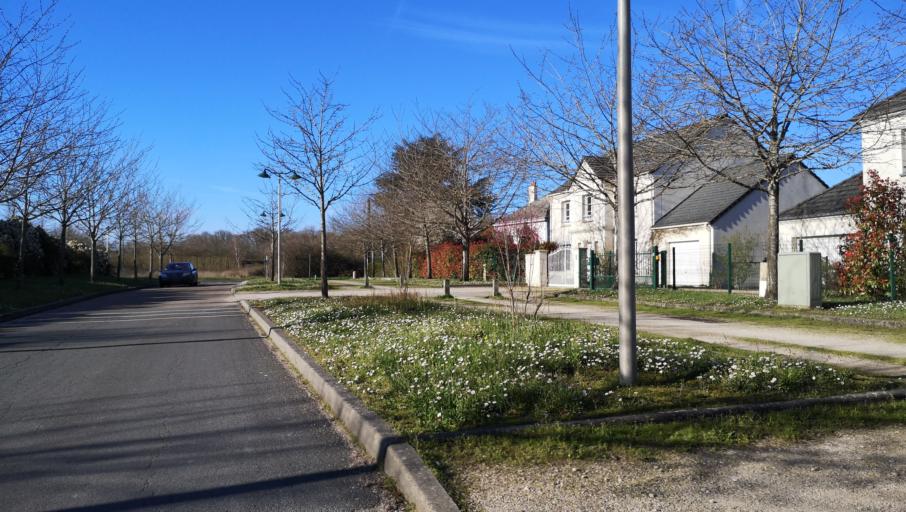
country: FR
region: Centre
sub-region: Departement du Loiret
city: Saint-Jean-de-Braye
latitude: 47.9120
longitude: 1.9866
